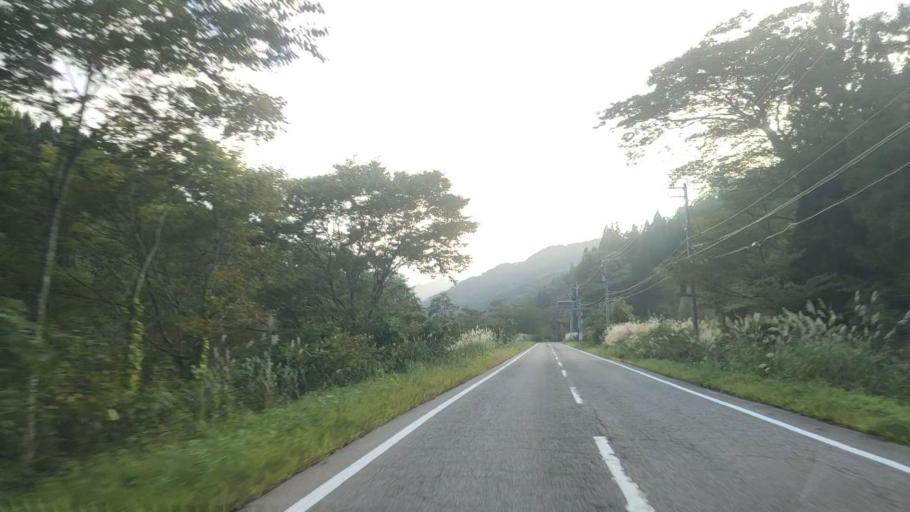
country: JP
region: Toyama
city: Yatsuomachi-higashikumisaka
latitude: 36.4642
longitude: 137.0461
